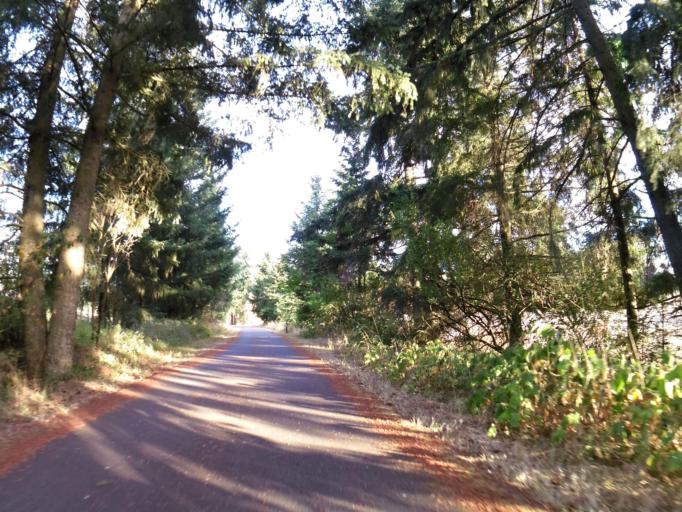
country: US
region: Washington
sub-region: Thurston County
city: Rainier
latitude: 46.8758
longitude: -122.7284
